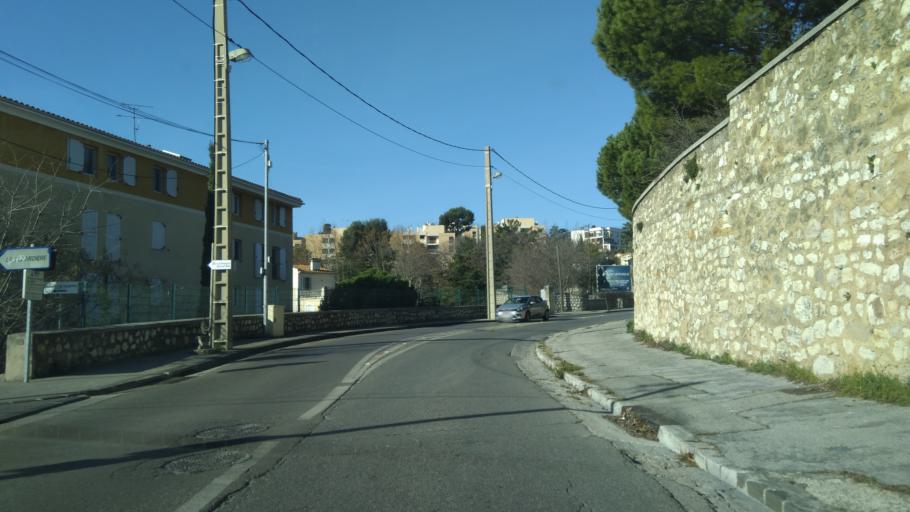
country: FR
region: Provence-Alpes-Cote d'Azur
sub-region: Departement des Bouches-du-Rhone
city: Marseille 12
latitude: 43.3034
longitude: 5.4420
